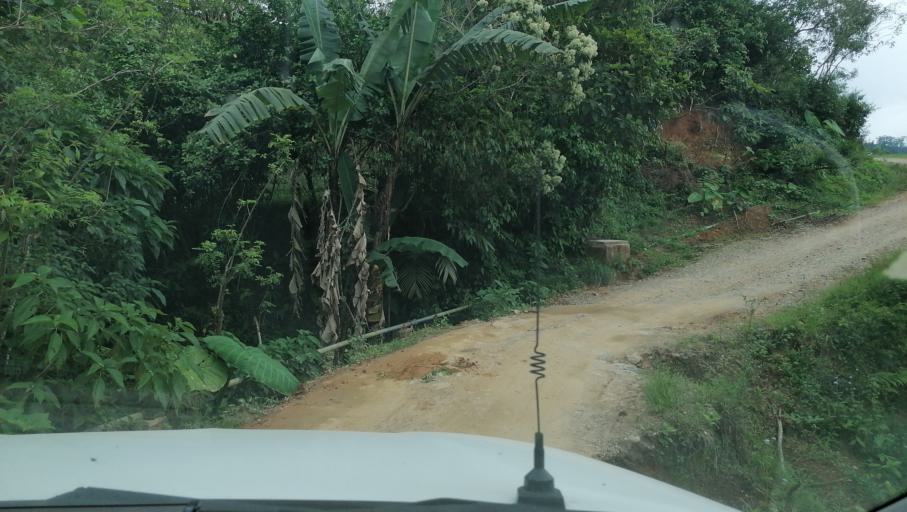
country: MX
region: Chiapas
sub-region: Francisco Leon
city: San Miguel la Sardina
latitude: 17.3360
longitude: -93.3134
